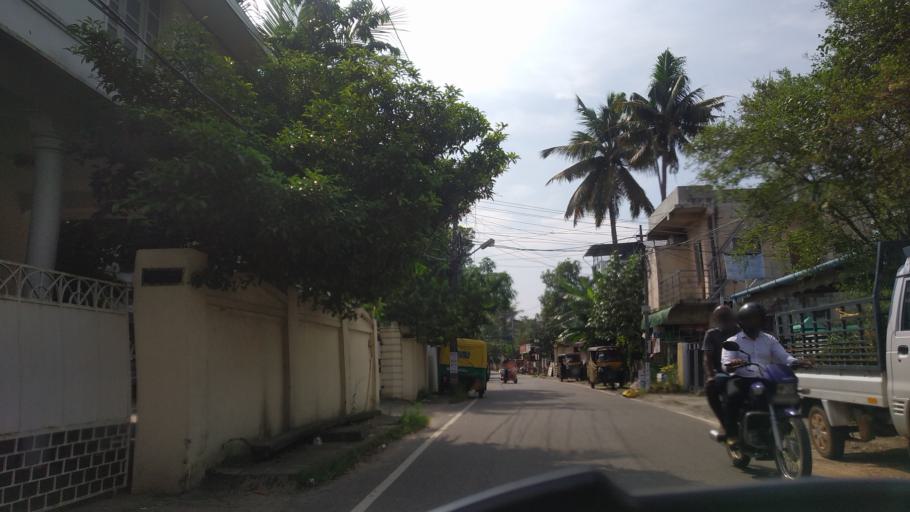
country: IN
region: Kerala
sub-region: Ernakulam
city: Elur
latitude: 10.0072
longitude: 76.2944
